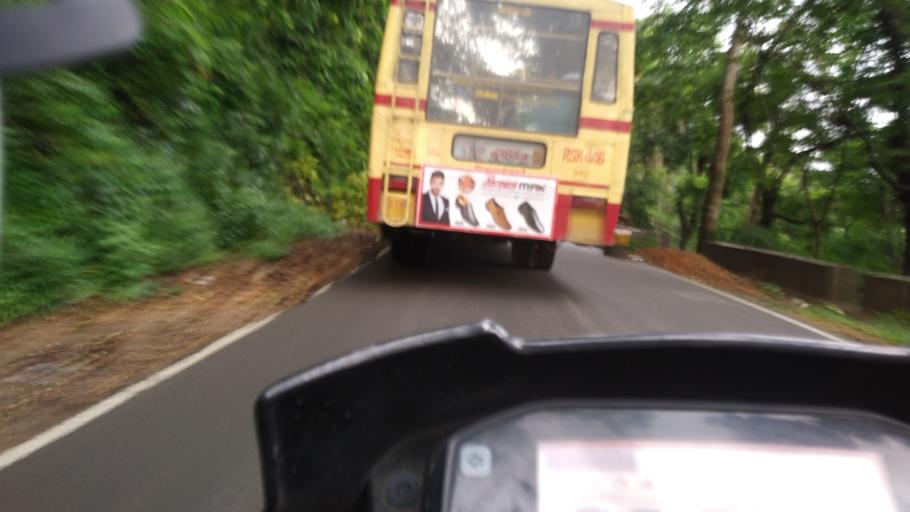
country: IN
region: Kerala
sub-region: Idukki
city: Kuttampuzha
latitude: 10.0661
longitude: 76.7745
